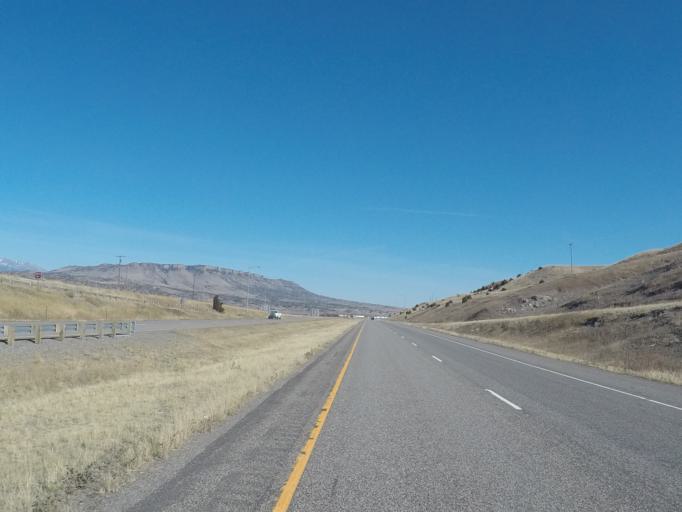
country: US
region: Montana
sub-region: Park County
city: Livingston
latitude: 45.7070
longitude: -110.4541
